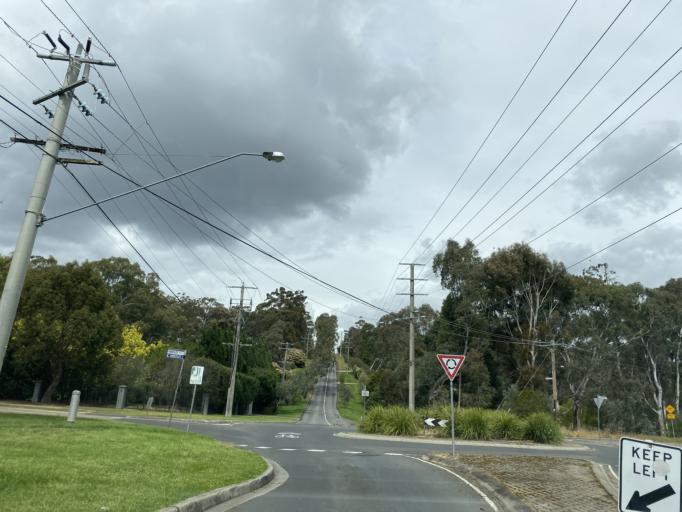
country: AU
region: Victoria
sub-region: Banyule
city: Lower Plenty
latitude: -37.7376
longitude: 145.1156
